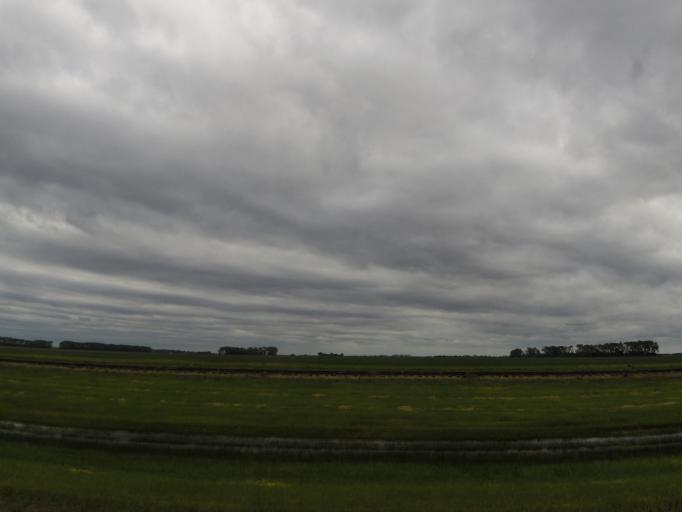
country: US
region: North Dakota
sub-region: Walsh County
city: Grafton
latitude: 48.5548
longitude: -97.4480
